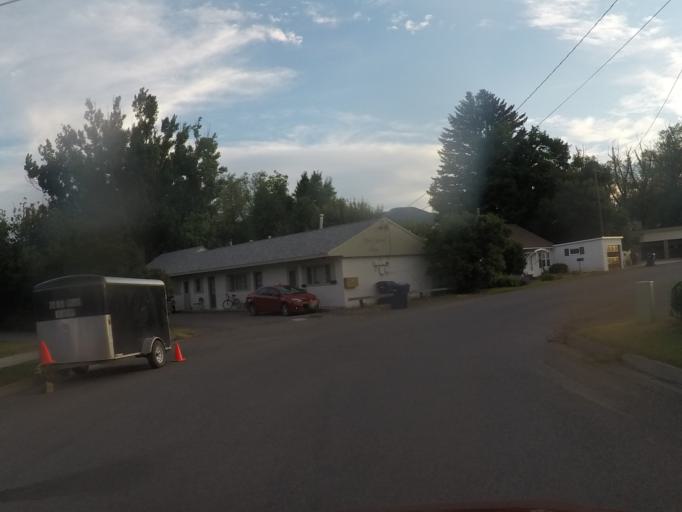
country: US
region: Montana
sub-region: Park County
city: Livingston
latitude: 45.6507
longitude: -110.5709
